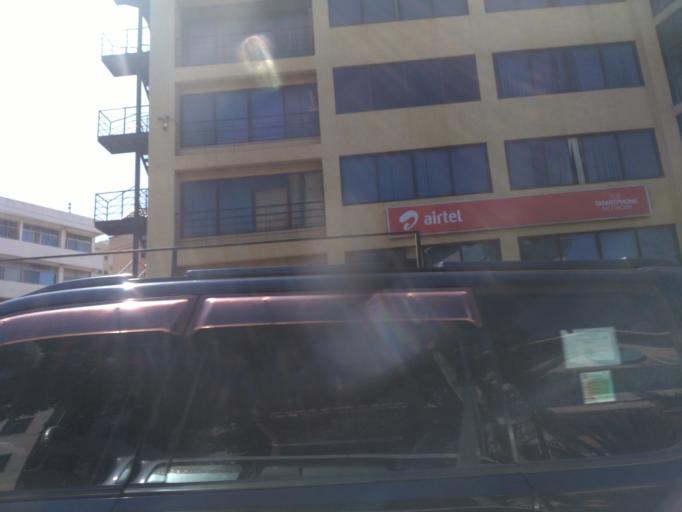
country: UG
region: Central Region
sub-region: Kampala District
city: Kampala
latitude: 0.3205
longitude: 32.5885
